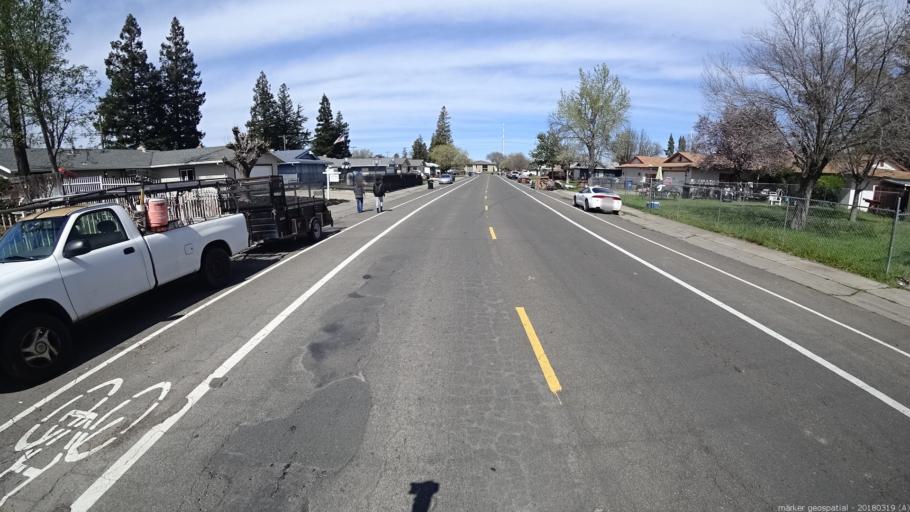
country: US
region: California
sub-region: Sacramento County
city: Parkway
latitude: 38.5058
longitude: -121.4503
